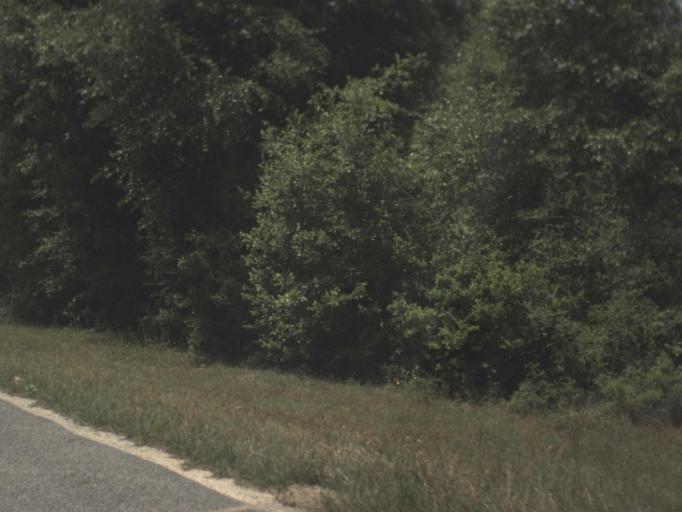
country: US
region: Florida
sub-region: Calhoun County
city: Blountstown
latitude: 30.5723
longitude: -85.1830
